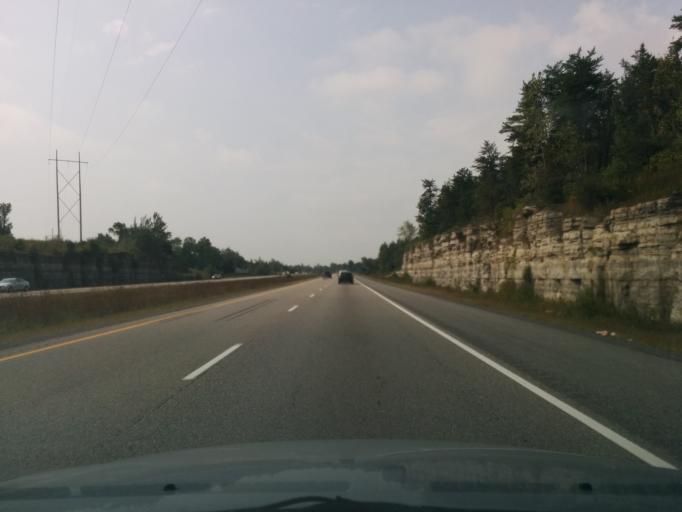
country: CA
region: Ontario
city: Bells Corners
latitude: 45.2942
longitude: -75.7970
